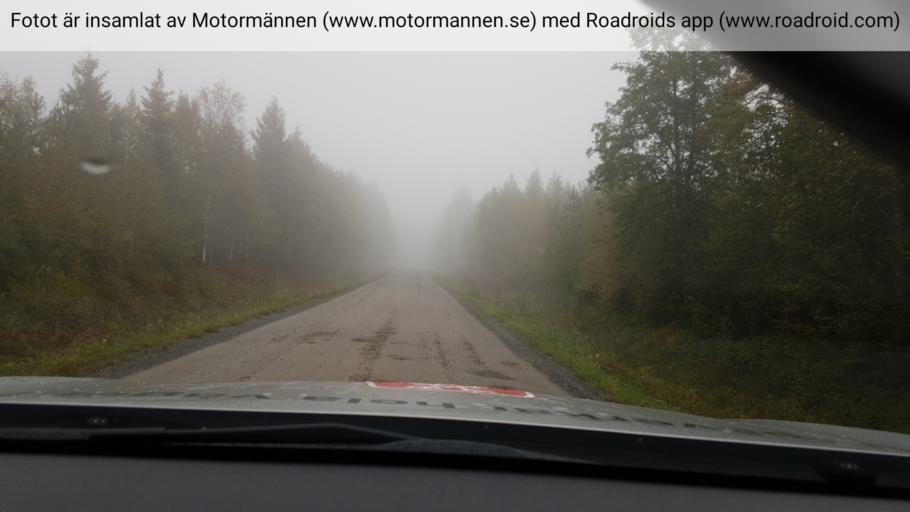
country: SE
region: Vaesterbotten
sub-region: Umea Kommun
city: Ersmark
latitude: 64.0896
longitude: 20.2265
